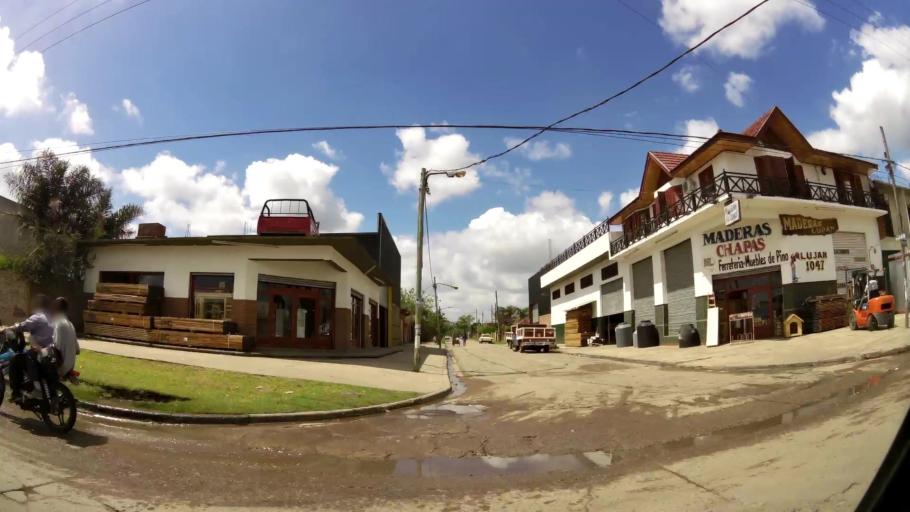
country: AR
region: Buenos Aires
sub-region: Partido de Quilmes
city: Quilmes
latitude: -34.8314
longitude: -58.2312
